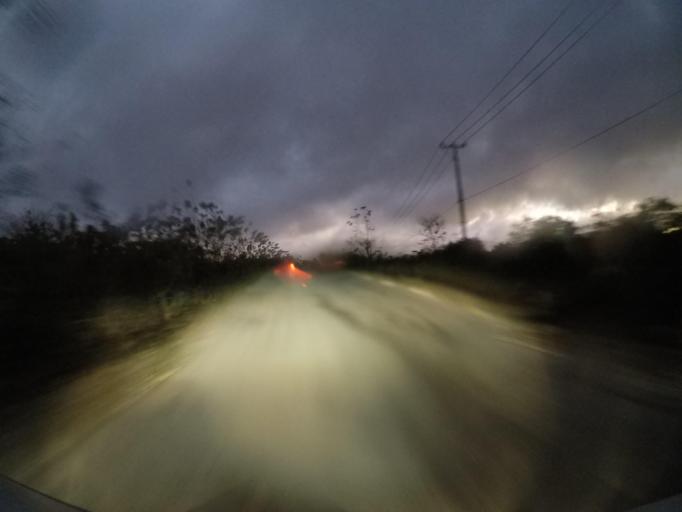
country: TL
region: Lautem
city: Lospalos
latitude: -8.4269
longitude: 127.0037
